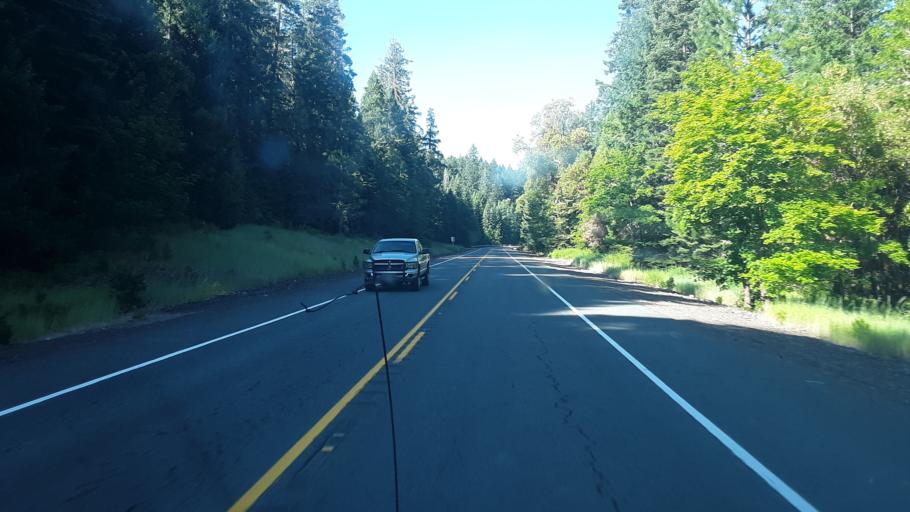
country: US
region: Oregon
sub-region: Jackson County
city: Shady Cove
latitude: 42.6782
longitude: -122.6188
